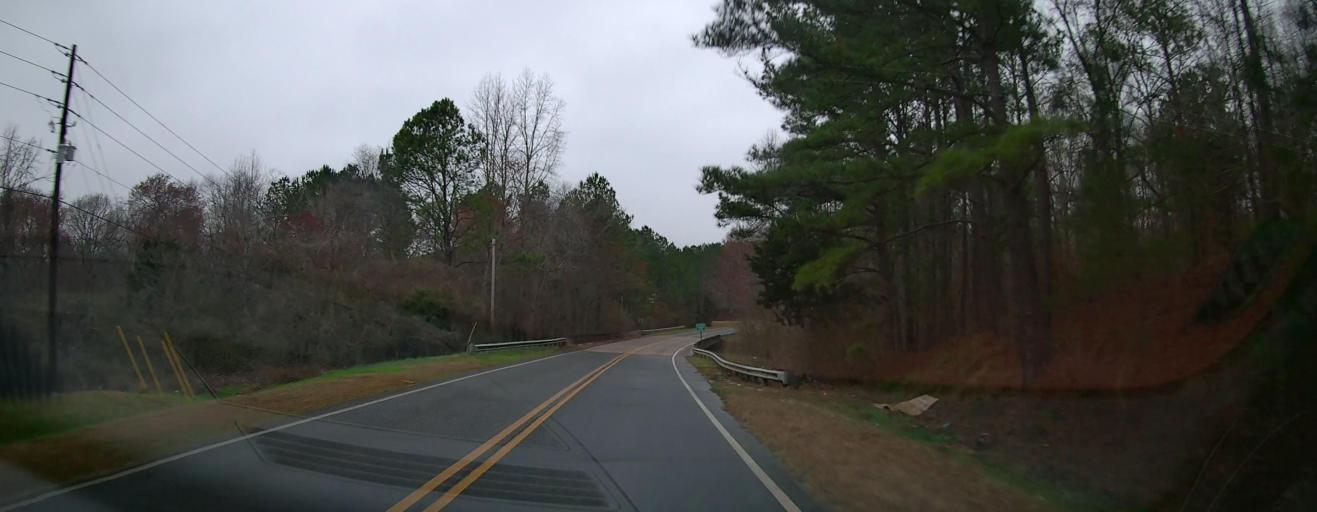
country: US
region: Georgia
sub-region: Pike County
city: Zebulon
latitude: 33.1247
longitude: -84.3459
